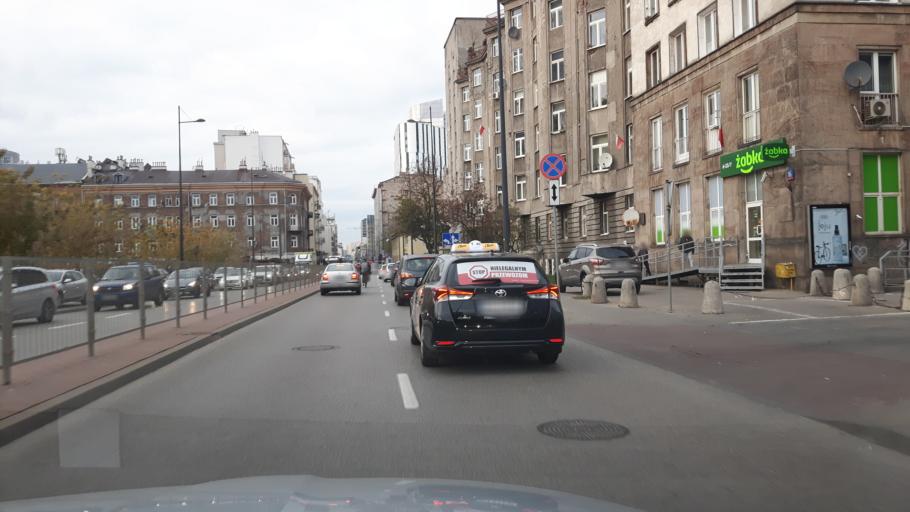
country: PL
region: Masovian Voivodeship
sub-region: Warszawa
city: Ochota
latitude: 52.2269
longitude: 20.9956
